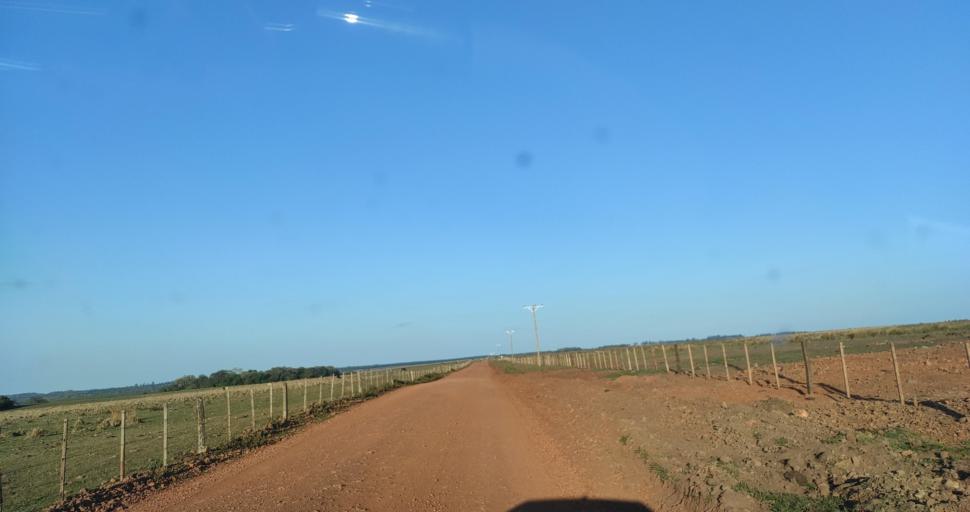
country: PY
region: Itapua
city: Carmen del Parana
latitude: -27.4085
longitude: -56.1612
